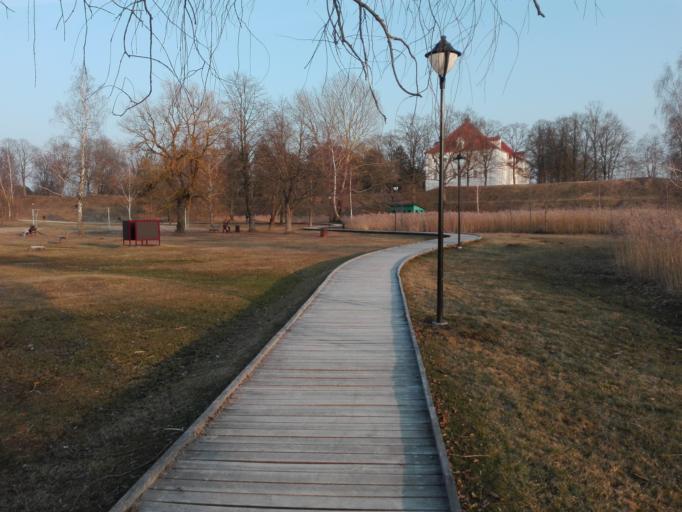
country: LT
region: Panevezys
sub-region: Birzai
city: Birzai
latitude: 56.2064
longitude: 24.7508
